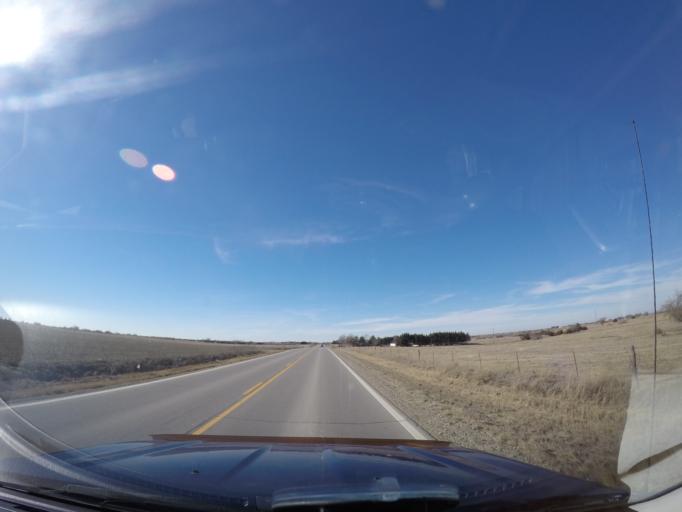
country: US
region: Kansas
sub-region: Dickinson County
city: Herington
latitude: 38.6674
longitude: -96.9136
